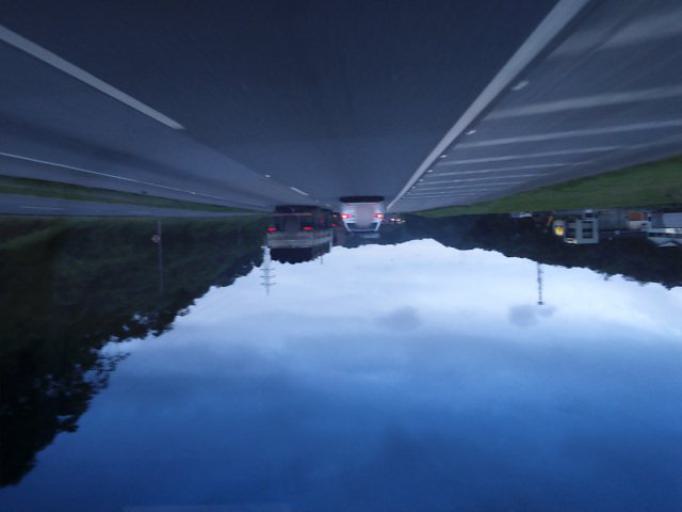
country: BR
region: Santa Catarina
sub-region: Joinville
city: Joinville
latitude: -26.3678
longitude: -48.8579
